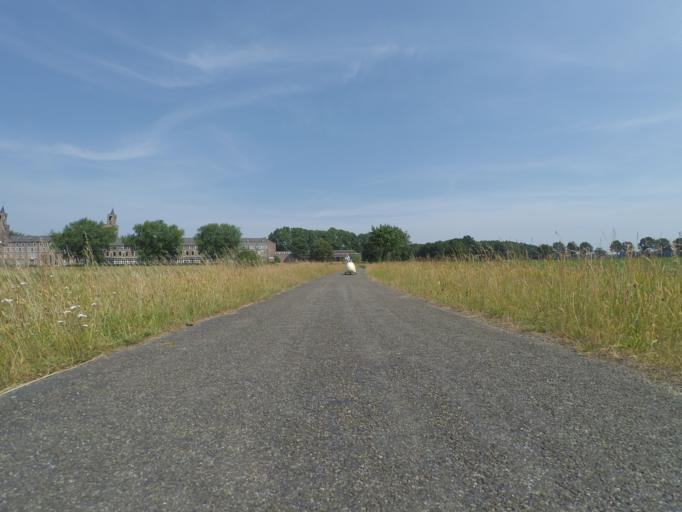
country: NL
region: North Brabant
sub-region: Gemeente Breda
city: Breda
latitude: 51.5377
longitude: 4.7811
